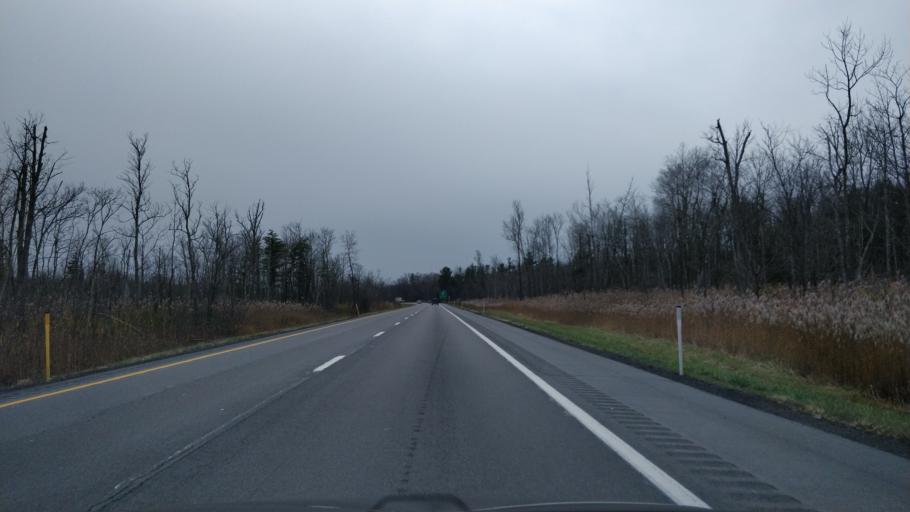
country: US
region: New York
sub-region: Jefferson County
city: Adams
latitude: 43.8345
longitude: -76.0288
